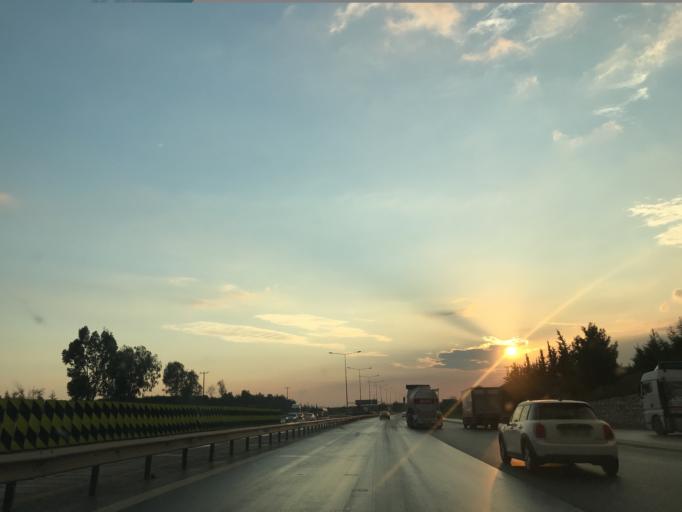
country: TR
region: Mersin
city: Yenice
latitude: 37.0286
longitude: 35.1133
